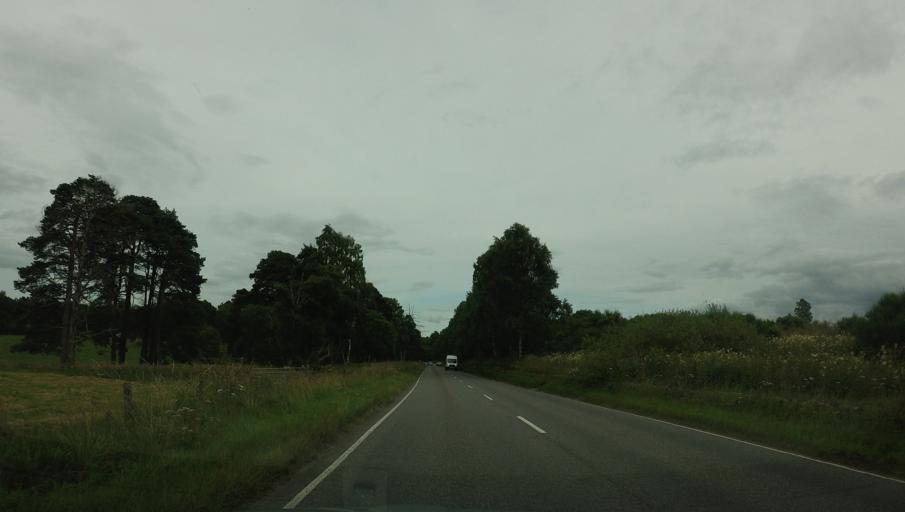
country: GB
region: Scotland
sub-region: Aberdeenshire
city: Aboyne
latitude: 57.0863
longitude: -2.7270
